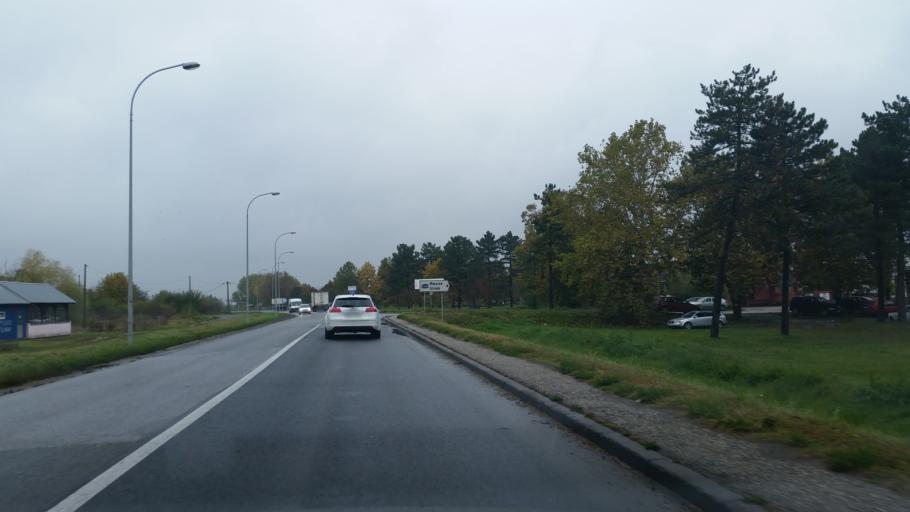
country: RS
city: Sefkerin
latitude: 44.9302
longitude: 20.4376
